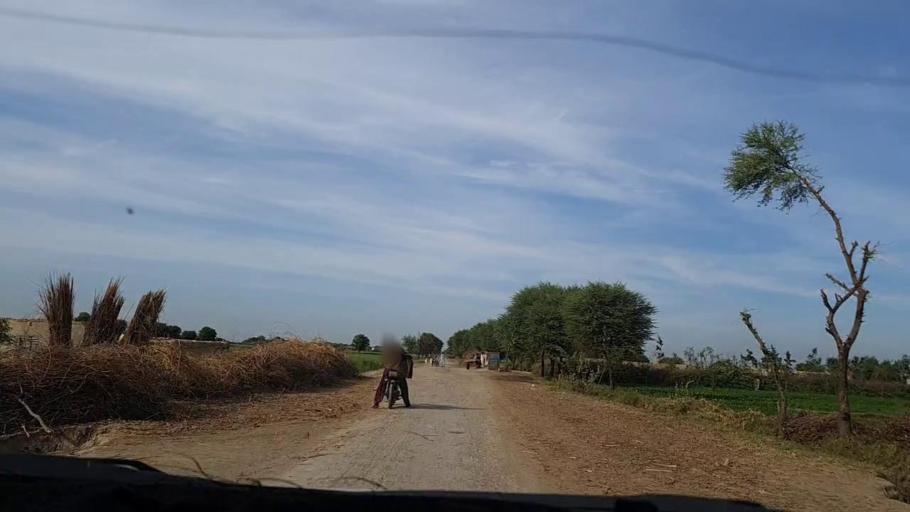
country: PK
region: Sindh
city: Dhoro Naro
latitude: 25.4417
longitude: 69.5122
